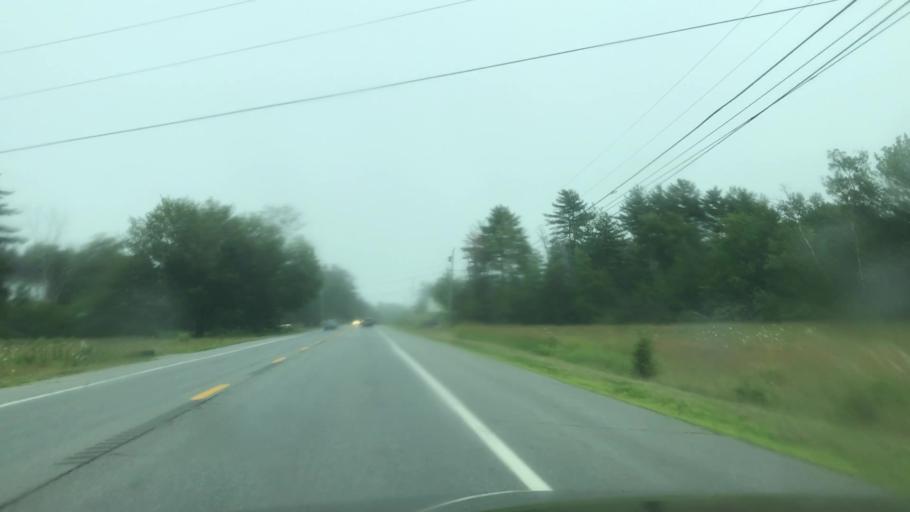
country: US
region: Maine
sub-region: Lincoln County
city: Nobleboro
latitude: 44.1027
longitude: -69.4448
